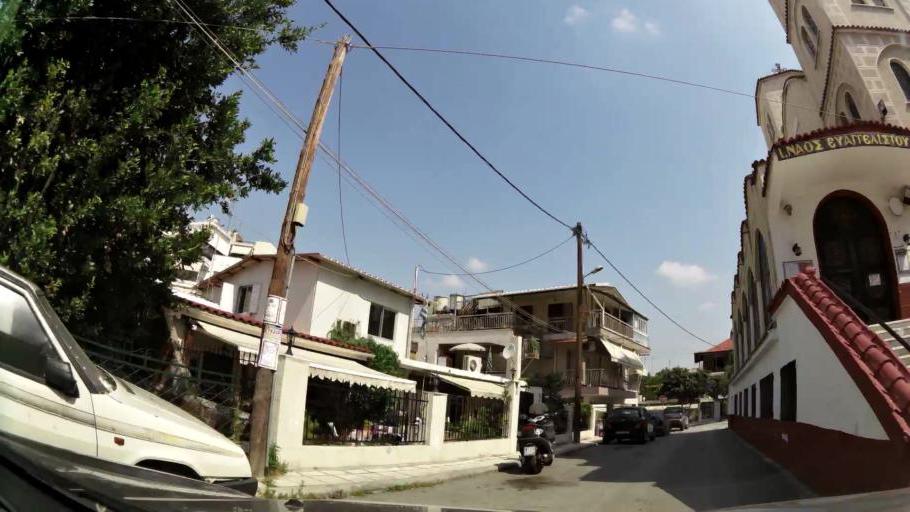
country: GR
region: Central Macedonia
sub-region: Nomos Thessalonikis
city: Stavroupoli
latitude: 40.6744
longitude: 22.9323
